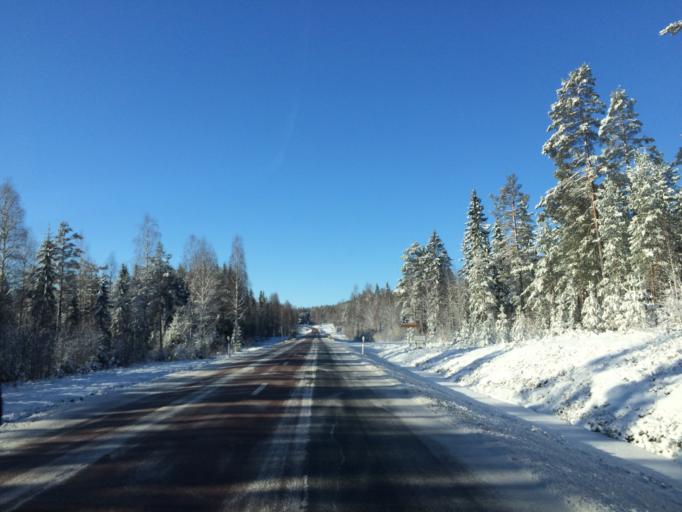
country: SE
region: Dalarna
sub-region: Mora Kommun
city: Mora
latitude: 60.8963
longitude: 14.3828
